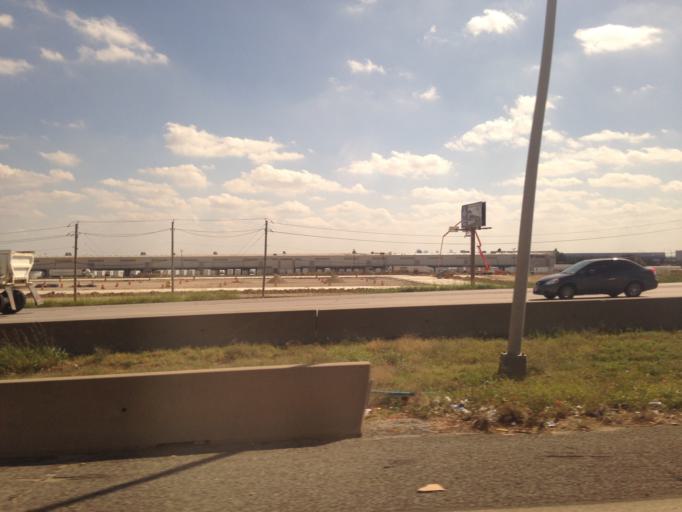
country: US
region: Texas
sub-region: Tarrant County
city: Saginaw
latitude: 32.8400
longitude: -97.3545
